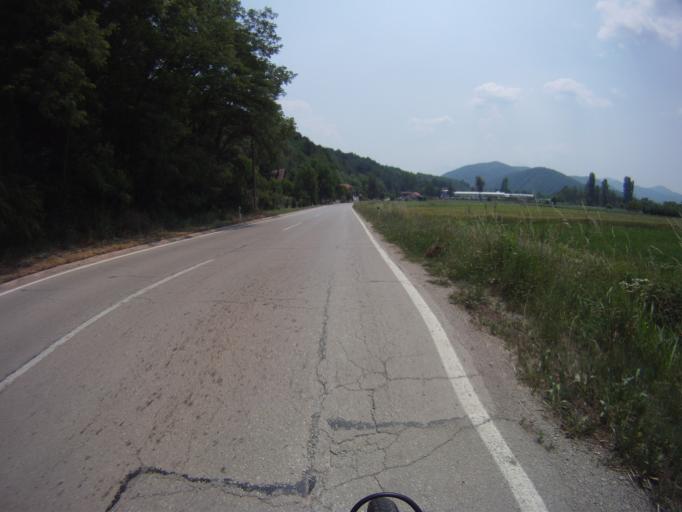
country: RS
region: Central Serbia
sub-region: Nisavski Okrug
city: Gadzin Han
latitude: 43.2327
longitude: 22.0289
